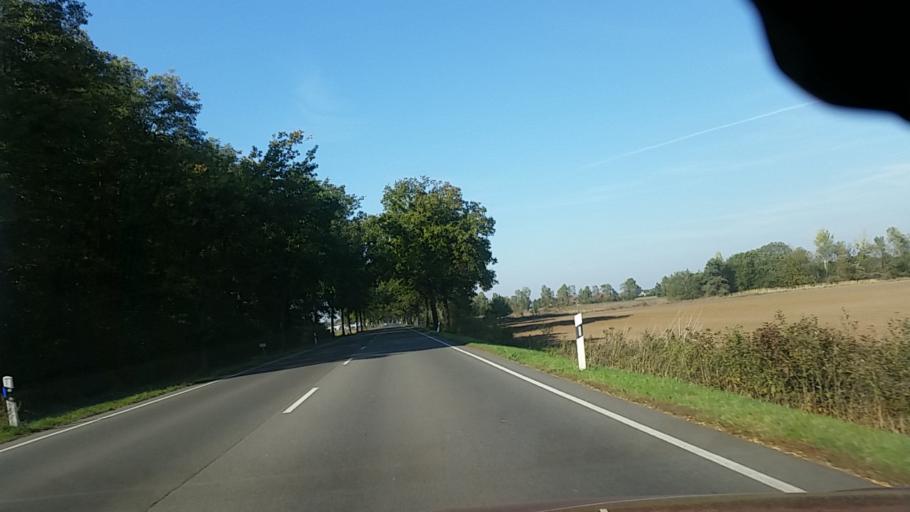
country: DE
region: Lower Saxony
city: Eicklingen
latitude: 52.5403
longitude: 10.2050
